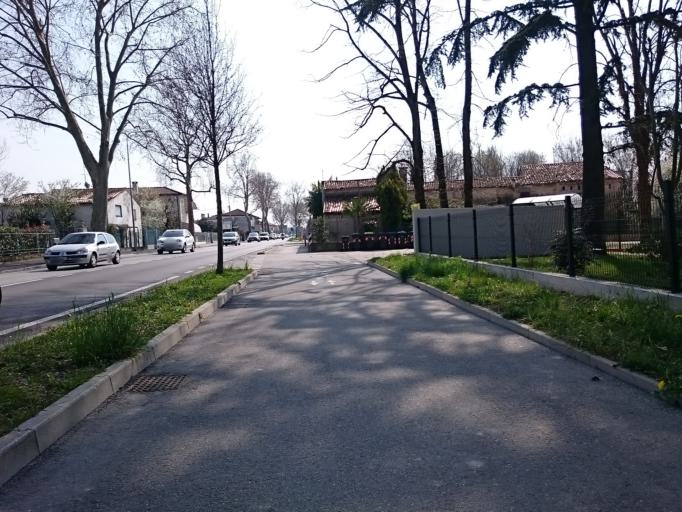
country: IT
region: Veneto
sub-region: Provincia di Padova
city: Albignasego
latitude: 45.3738
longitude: 11.8872
